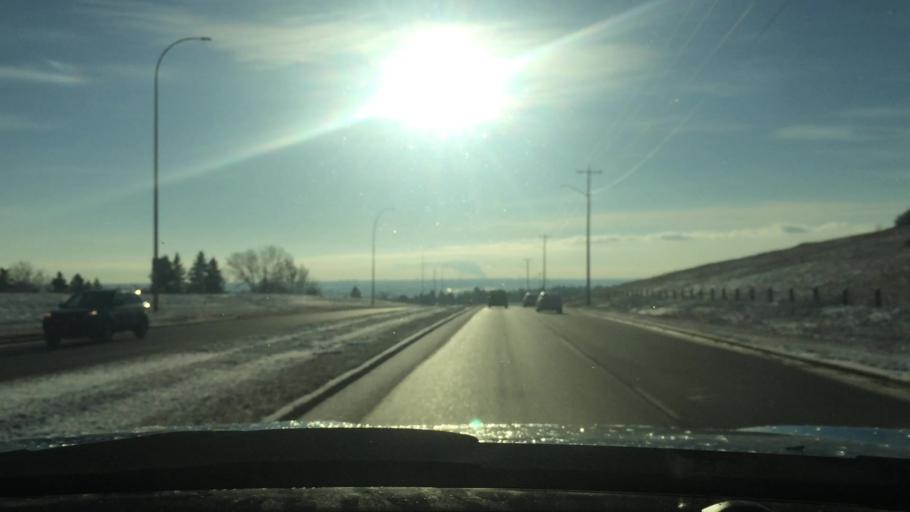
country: CA
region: Alberta
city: Calgary
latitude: 51.1198
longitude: -114.0899
